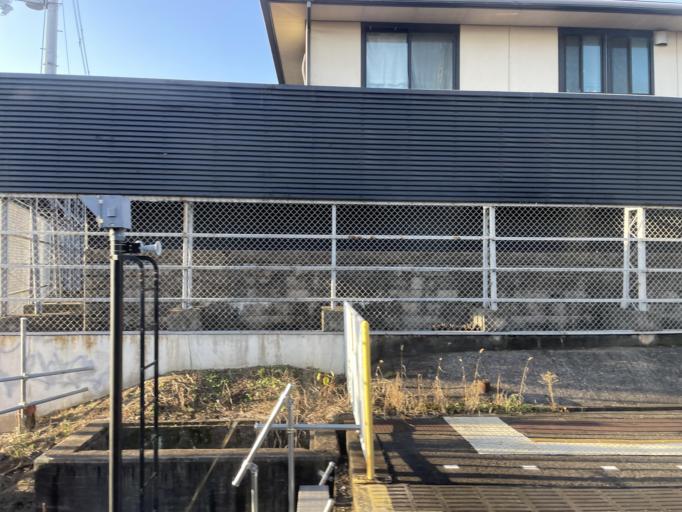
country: JP
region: Osaka
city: Kashihara
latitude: 34.5715
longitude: 135.6160
